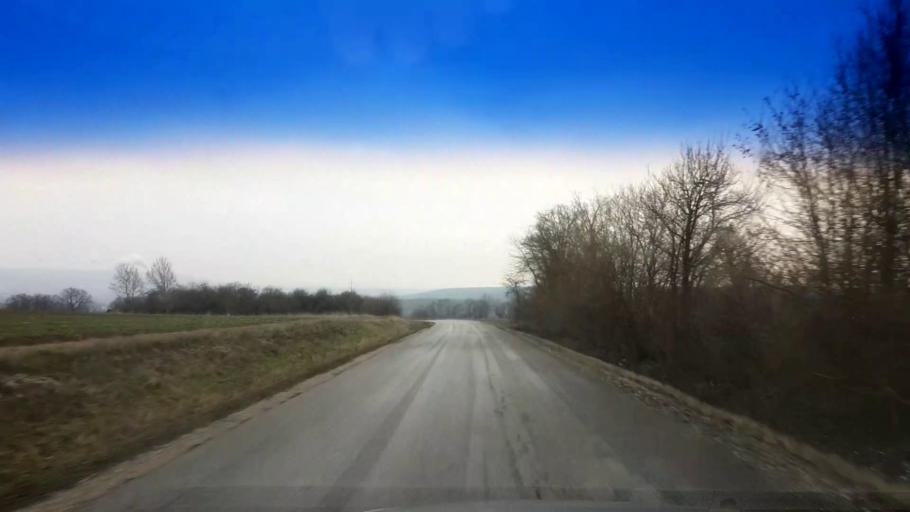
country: DE
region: Bavaria
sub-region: Upper Franconia
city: Hallerndorf
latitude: 49.7744
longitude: 10.9884
